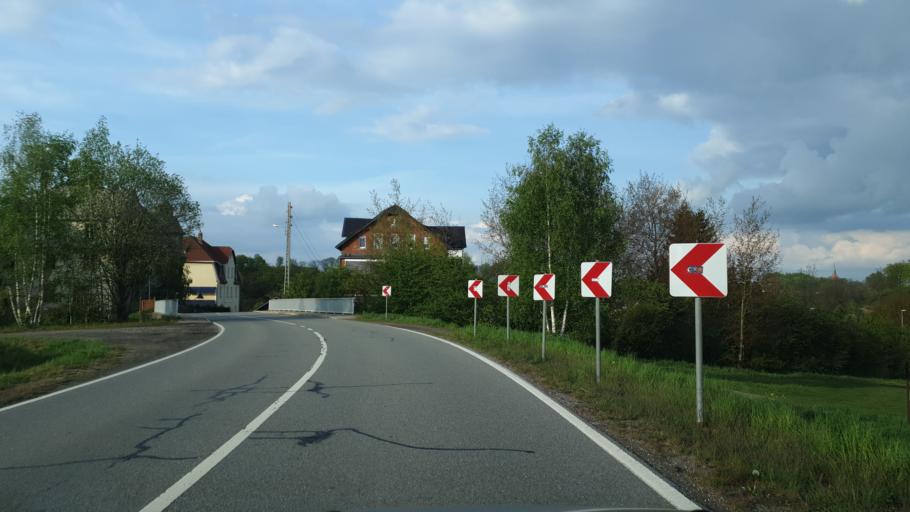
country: DE
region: Saxony
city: Lichtenstein
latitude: 50.7420
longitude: 12.6529
